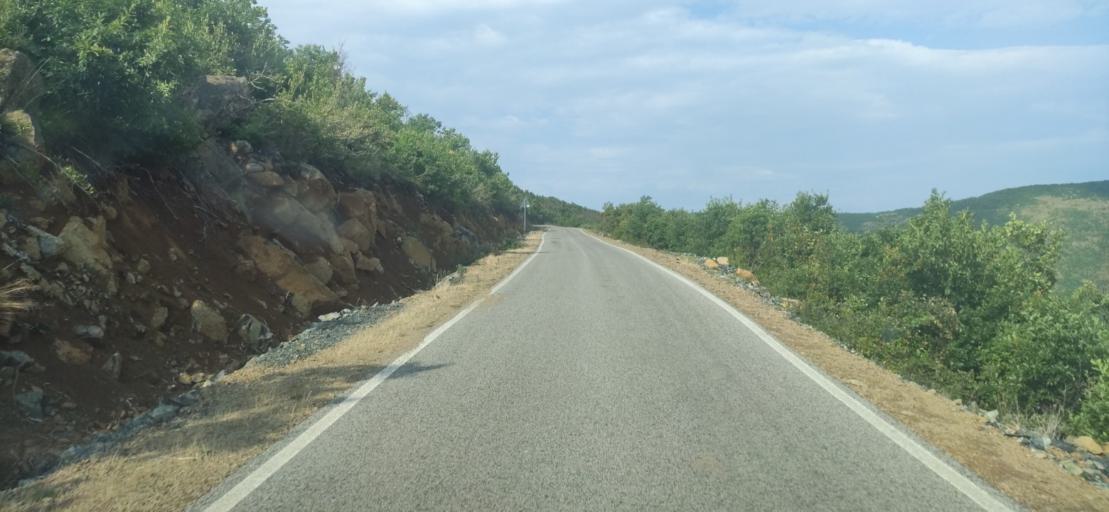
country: AL
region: Shkoder
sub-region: Rrethi i Pukes
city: Iballe
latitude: 42.1743
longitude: 19.9962
